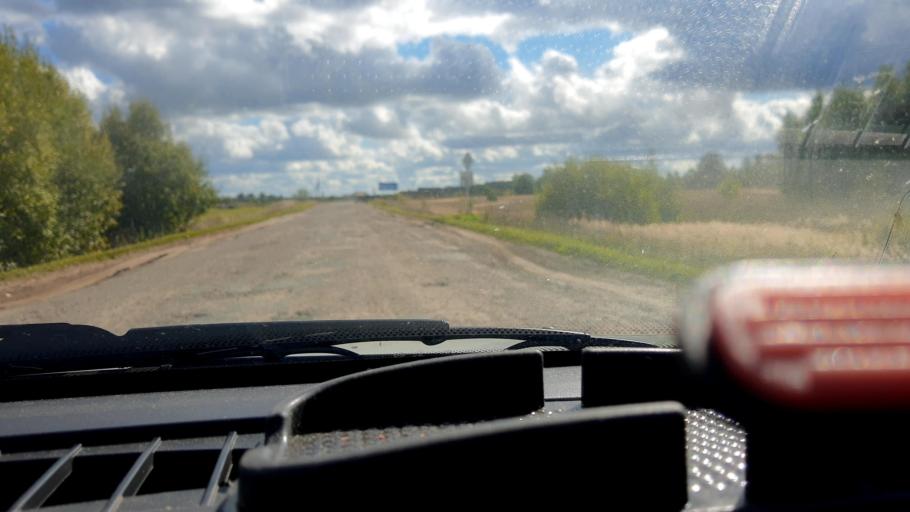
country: RU
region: Nizjnij Novgorod
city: Sharanga
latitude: 56.9391
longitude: 46.6498
